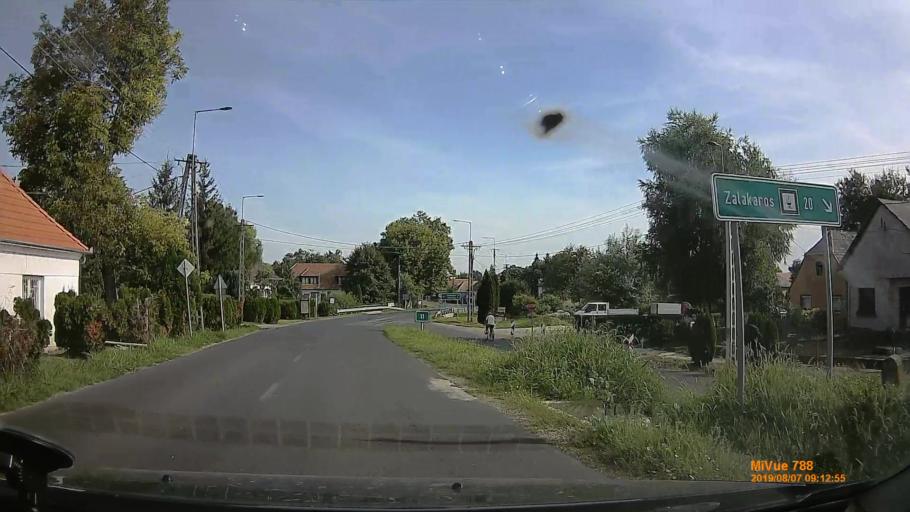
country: HU
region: Zala
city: Sarmellek
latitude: 46.7254
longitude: 17.1063
